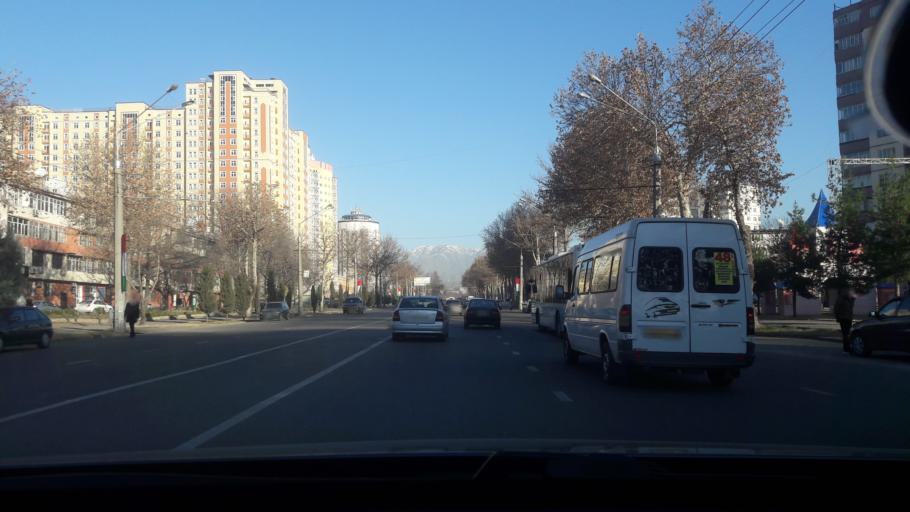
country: TJ
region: Dushanbe
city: Dushanbe
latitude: 38.5598
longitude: 68.7550
